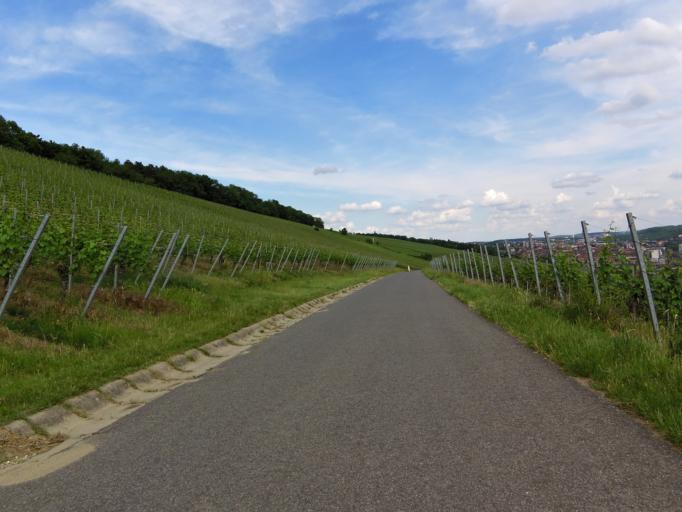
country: DE
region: Bavaria
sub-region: Regierungsbezirk Unterfranken
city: Wuerzburg
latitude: 49.8063
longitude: 9.9241
